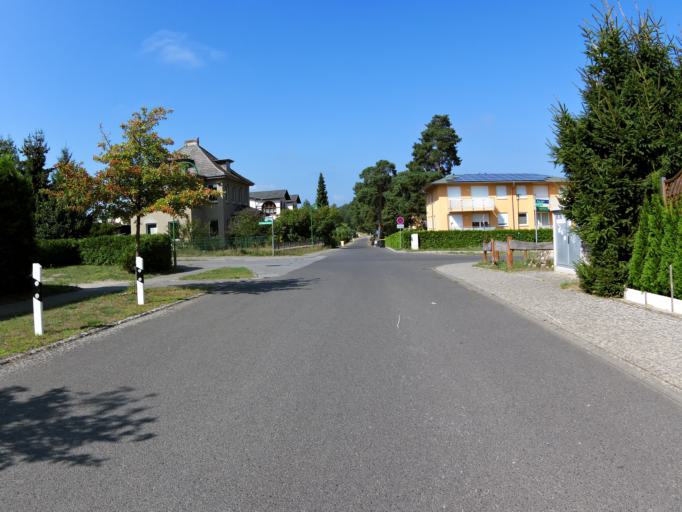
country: DE
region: Mecklenburg-Vorpommern
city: Loddin
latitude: 54.0164
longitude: 14.0520
